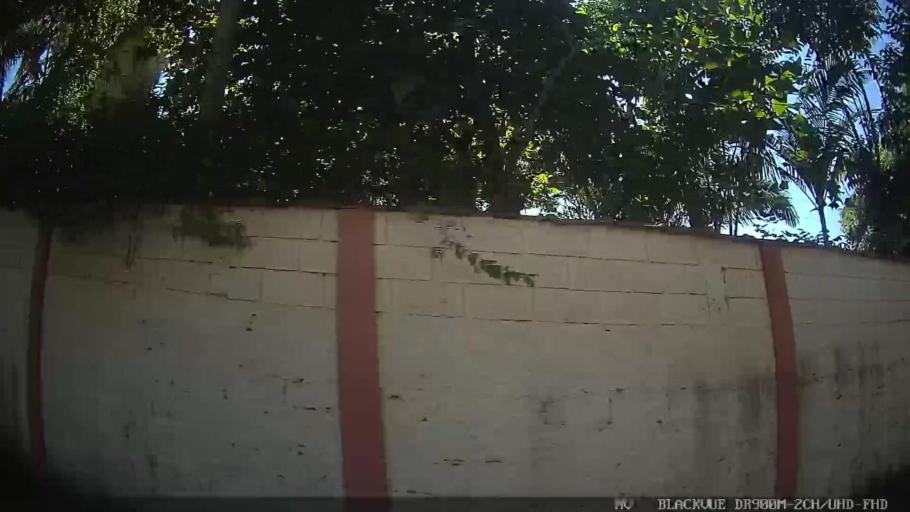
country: BR
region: Sao Paulo
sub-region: Atibaia
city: Atibaia
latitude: -23.1093
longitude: -46.5950
